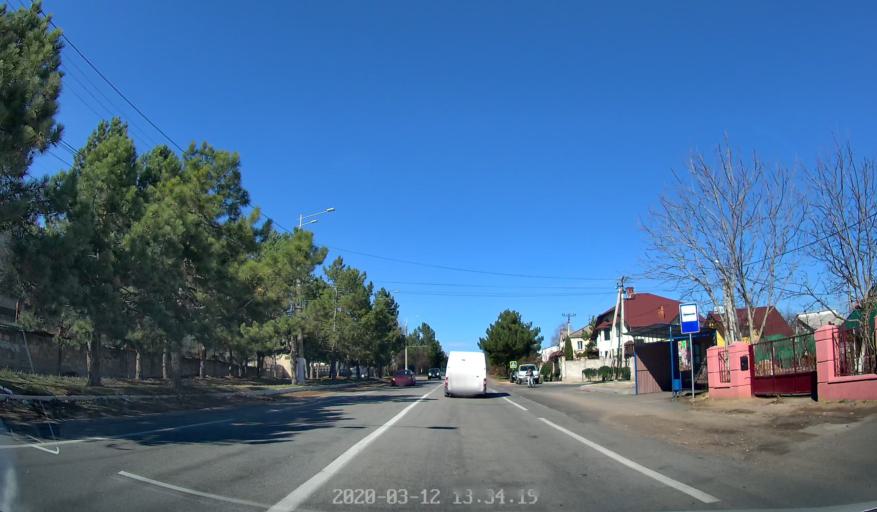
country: MD
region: Laloveni
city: Ialoveni
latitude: 46.9626
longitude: 28.7674
